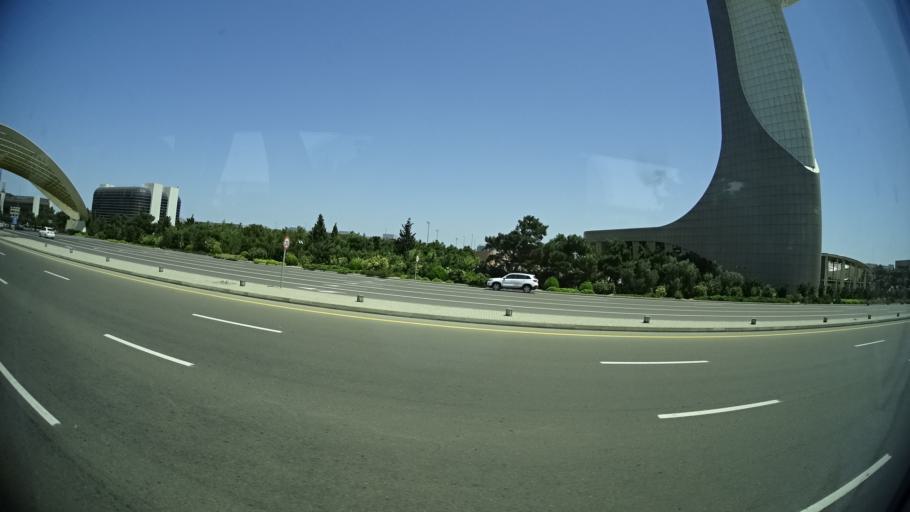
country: AZ
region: Baki
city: Yeni Suraxani
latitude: 40.4557
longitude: 50.0523
